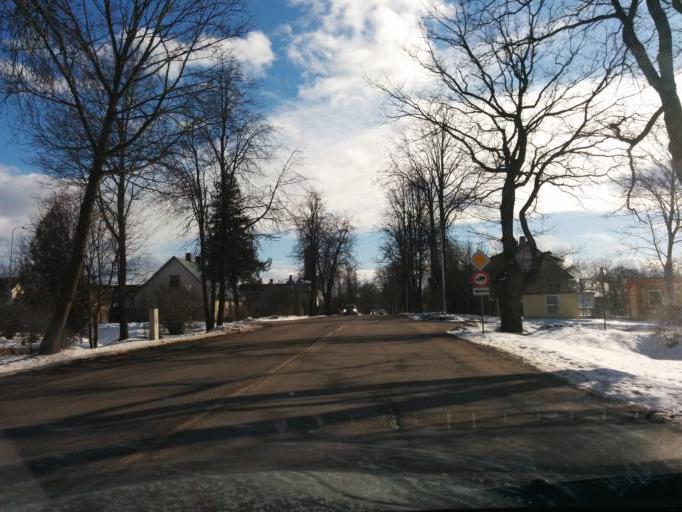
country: LV
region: Gulbenes Rajons
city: Gulbene
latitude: 57.1696
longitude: 26.7513
